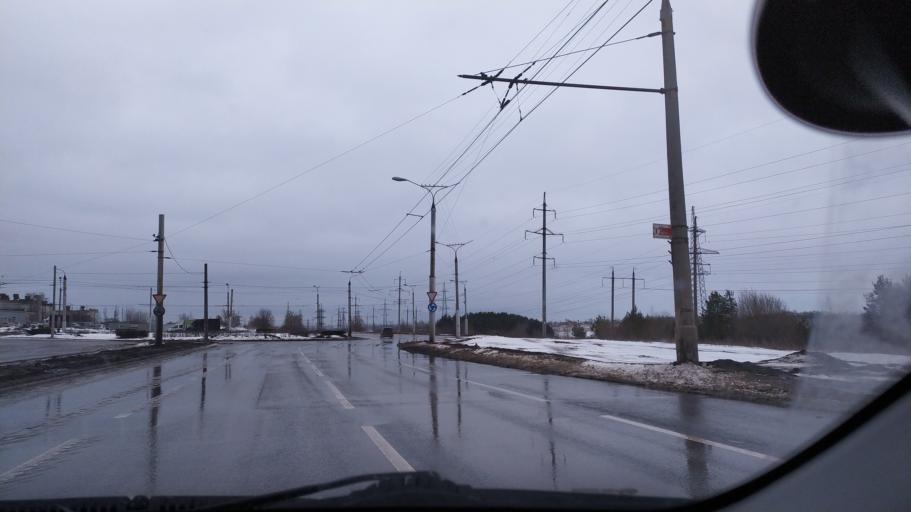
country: RU
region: Chuvashia
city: Kugesi
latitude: 56.1132
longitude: 47.3576
